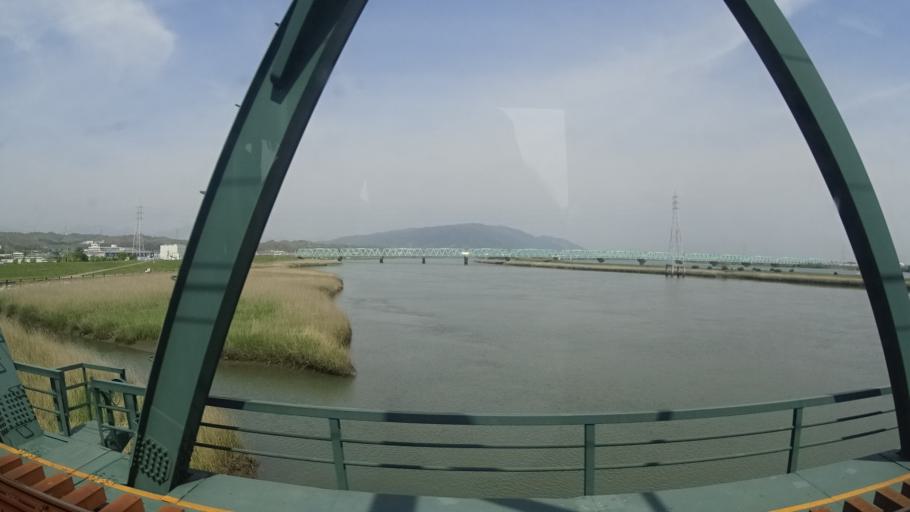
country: JP
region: Aichi
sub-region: Tsushima-shi
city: Tsushima
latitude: 35.0898
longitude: 136.6813
